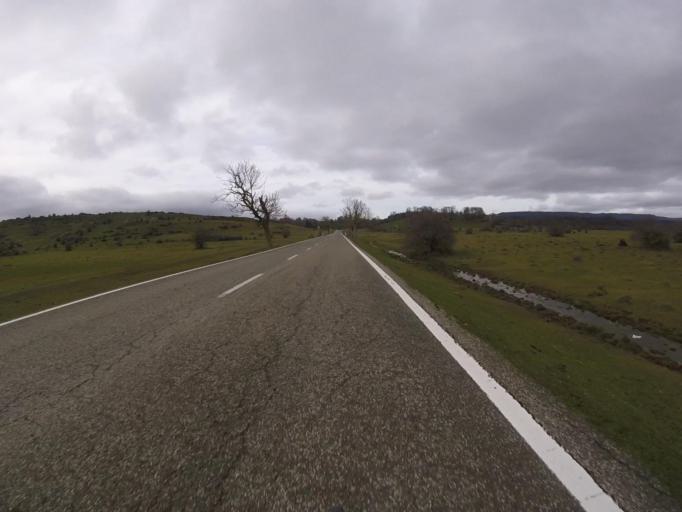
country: ES
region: Navarre
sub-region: Provincia de Navarra
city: Eulate
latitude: 42.8137
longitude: -2.1630
